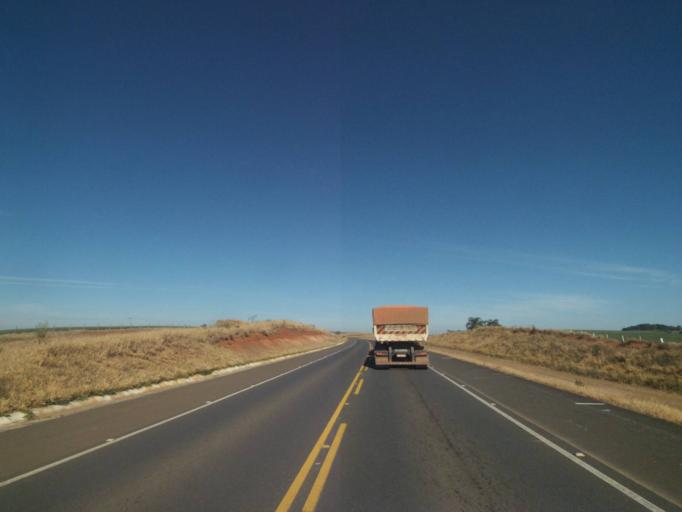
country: BR
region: Parana
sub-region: Tibagi
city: Tibagi
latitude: -24.6261
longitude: -50.4534
